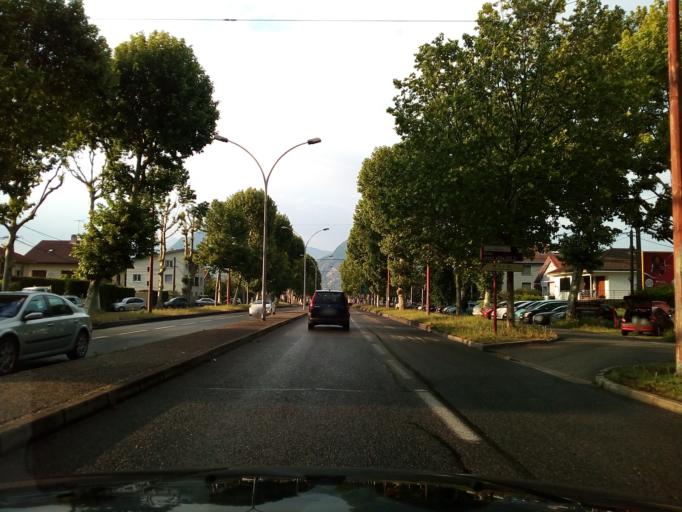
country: FR
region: Rhone-Alpes
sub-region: Departement de l'Isere
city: Grenoble
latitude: 45.1547
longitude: 5.7079
